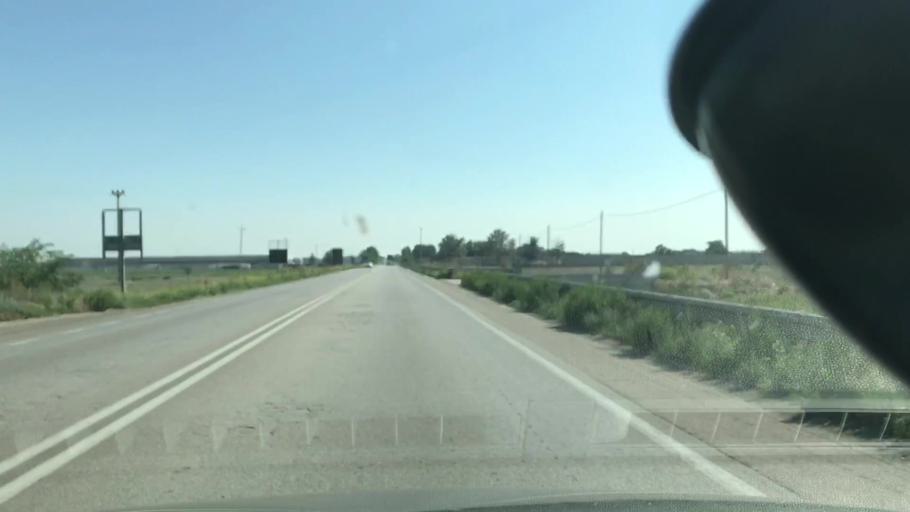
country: IT
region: Apulia
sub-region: Provincia di Foggia
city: Foggia
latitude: 41.4271
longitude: 15.5692
